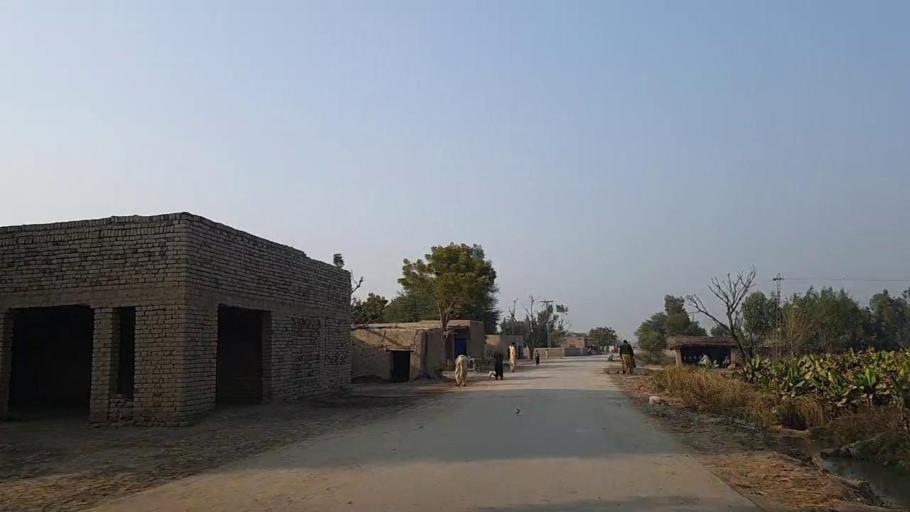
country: PK
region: Sindh
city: Sann
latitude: 26.1235
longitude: 68.1467
